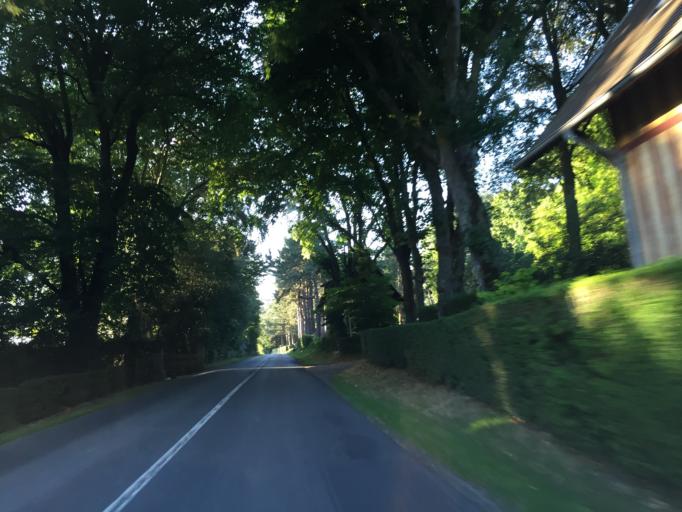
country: FR
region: Lower Normandy
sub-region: Departement du Calvados
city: Equemauville
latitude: 49.4036
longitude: 0.1795
